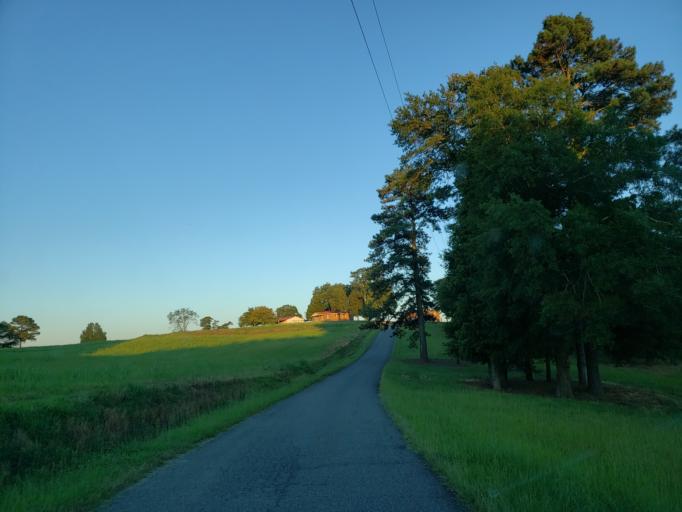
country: US
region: Georgia
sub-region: Bartow County
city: Euharlee
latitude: 34.1091
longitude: -84.8821
